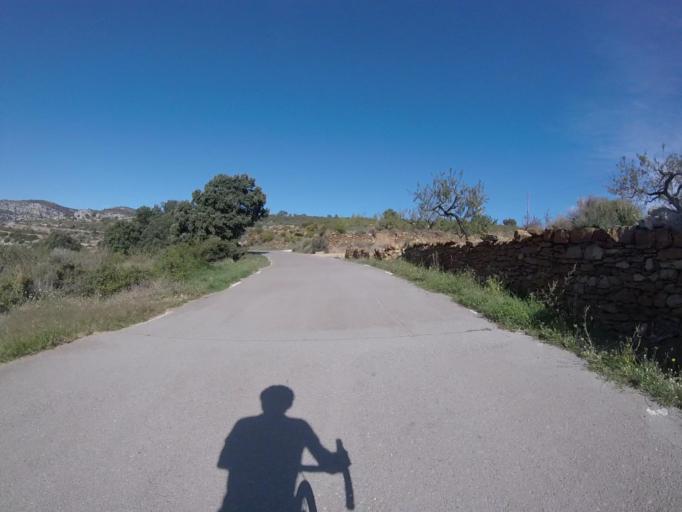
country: ES
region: Valencia
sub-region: Provincia de Castello
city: Sarratella
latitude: 40.2959
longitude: 0.0308
